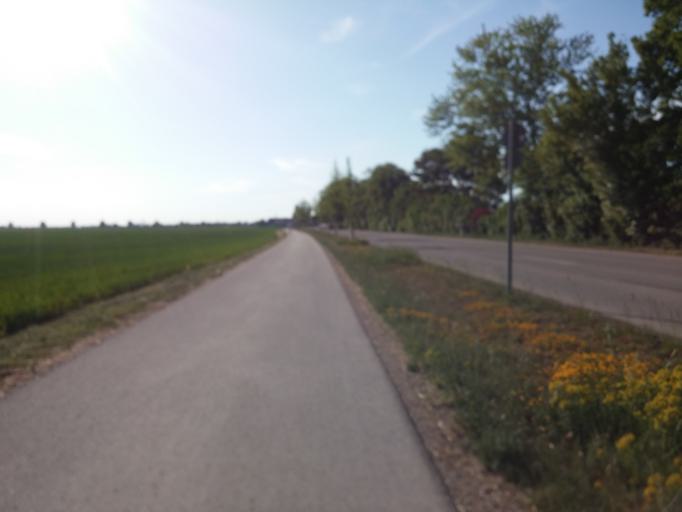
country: DE
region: Bavaria
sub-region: Upper Bavaria
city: Vaterstetten
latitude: 48.1232
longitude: 11.7512
